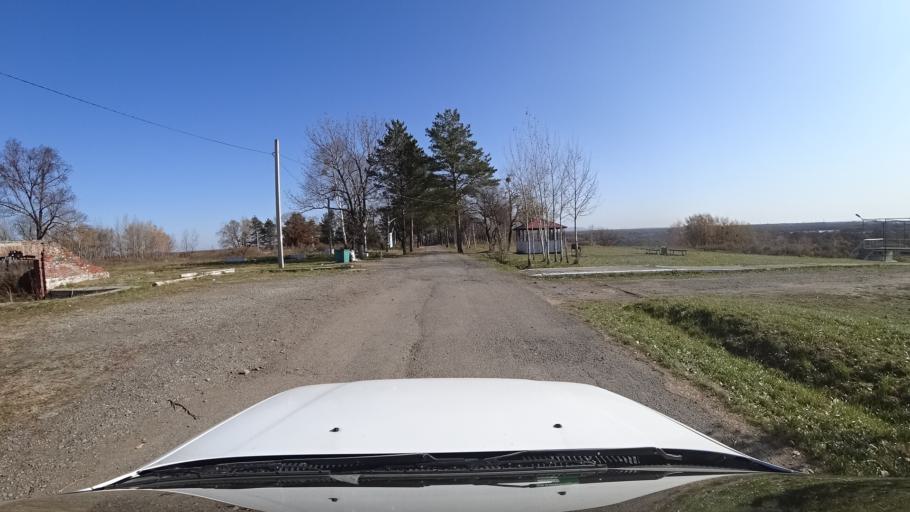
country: RU
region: Primorskiy
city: Dal'nerechensk
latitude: 45.9455
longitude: 133.6863
